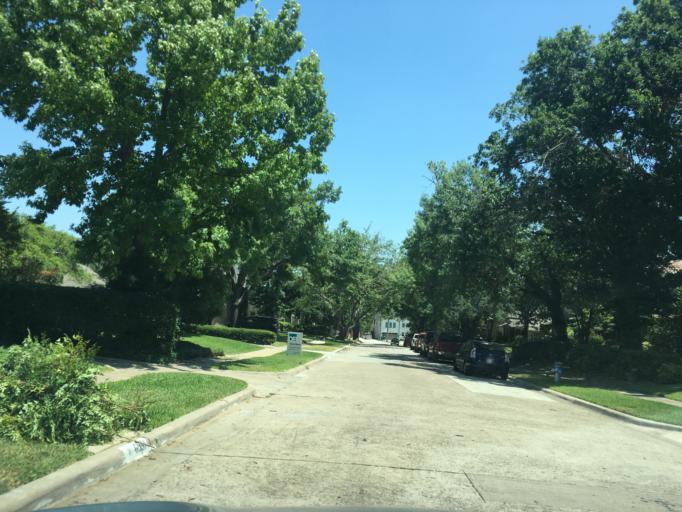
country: US
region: Texas
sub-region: Dallas County
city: Highland Park
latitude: 32.8331
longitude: -96.7420
